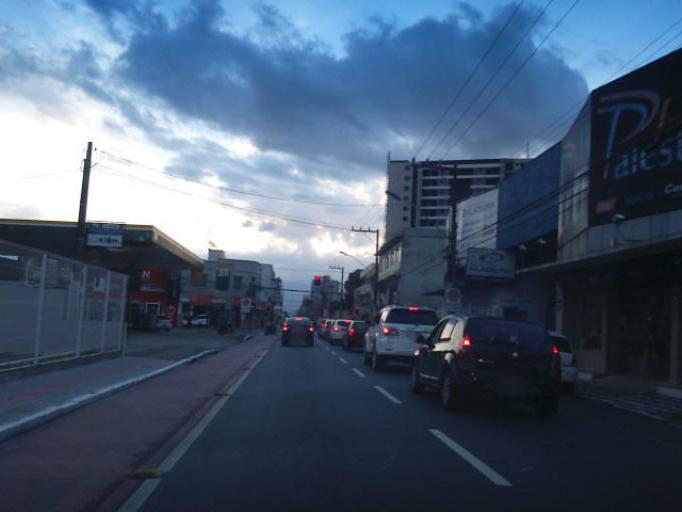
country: BR
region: Santa Catarina
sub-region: Itajai
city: Itajai
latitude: -26.9041
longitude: -48.6642
